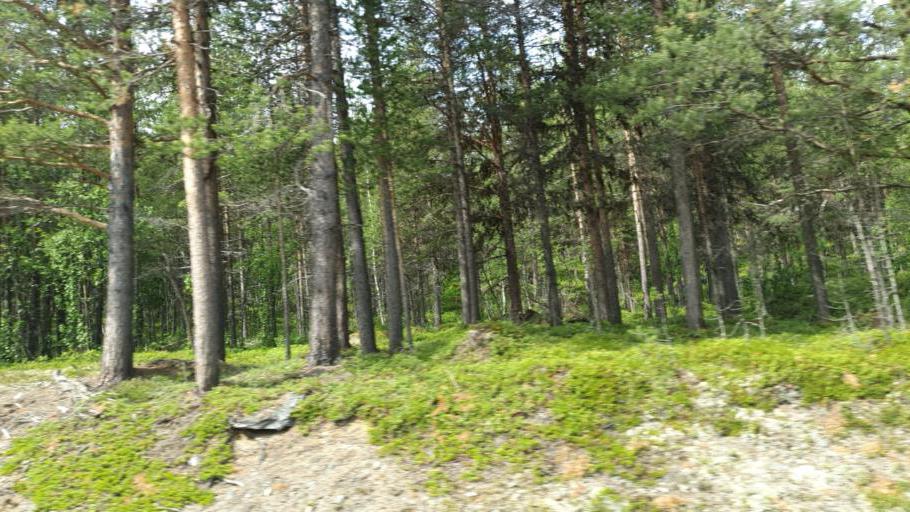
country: NO
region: Oppland
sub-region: Vaga
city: Vagamo
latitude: 61.6822
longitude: 9.0571
